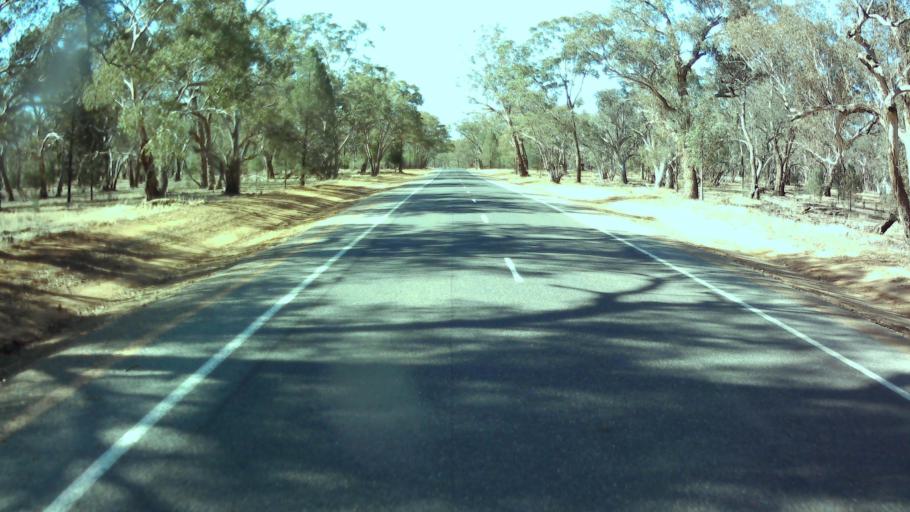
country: AU
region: New South Wales
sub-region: Weddin
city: Grenfell
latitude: -33.7623
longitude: 148.0820
